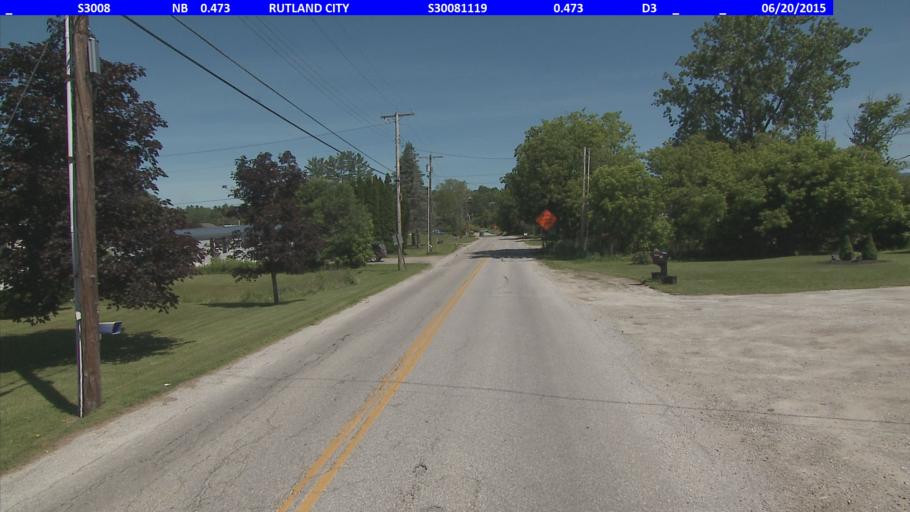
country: US
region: Vermont
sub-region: Rutland County
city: Rutland
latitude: 43.5933
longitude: -72.9926
